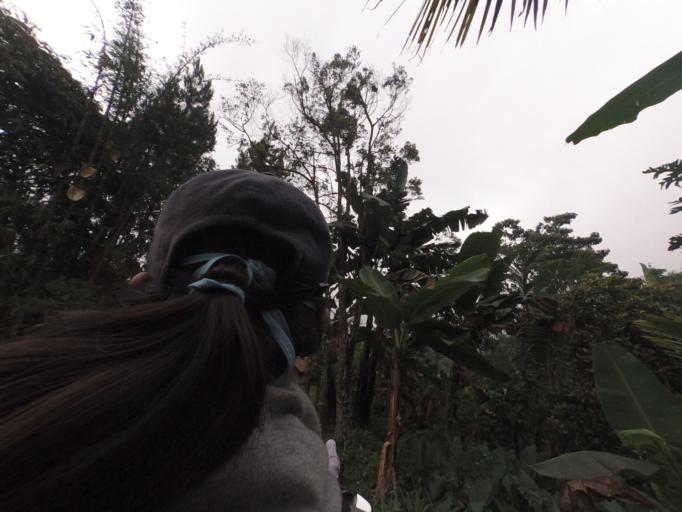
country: ID
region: West Java
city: Cicurug
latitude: -6.7010
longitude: 106.6610
